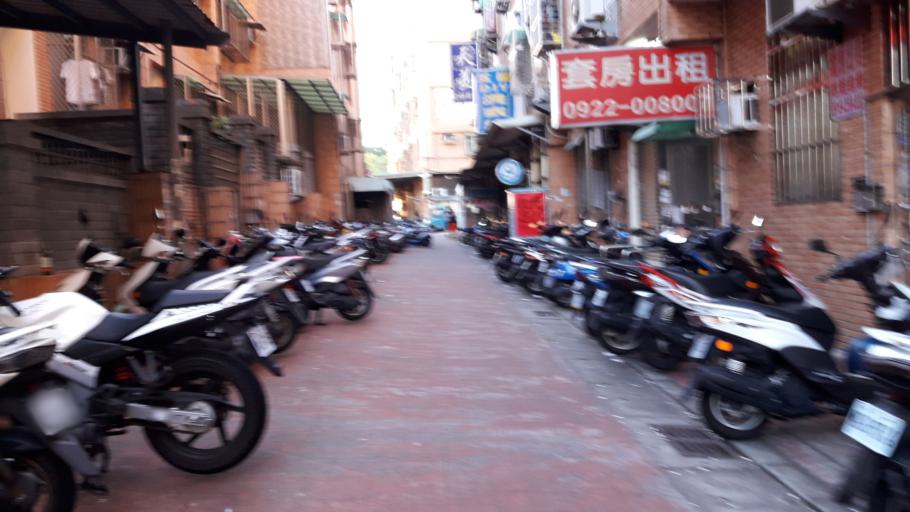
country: TW
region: Taiwan
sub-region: Hsinchu
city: Hsinchu
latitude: 24.7563
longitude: 120.9524
